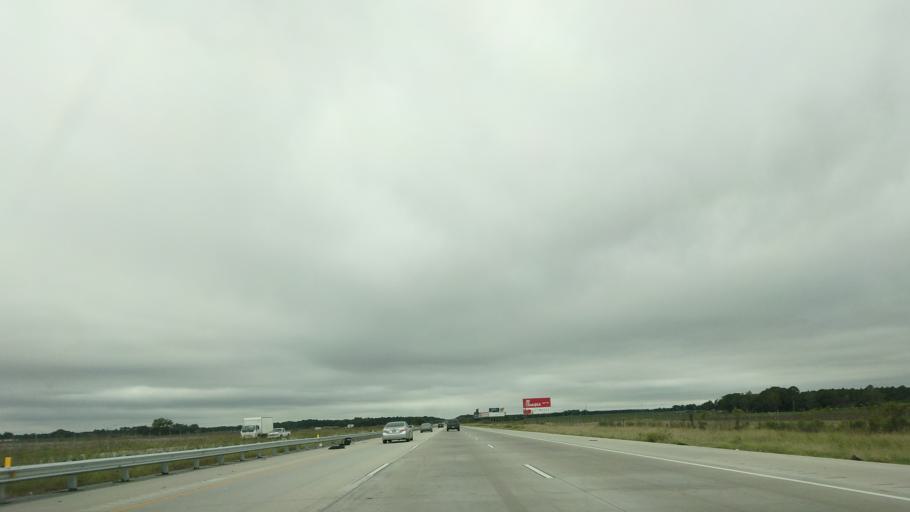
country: US
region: Georgia
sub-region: Dooly County
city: Vienna
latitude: 32.1541
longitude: -83.7557
